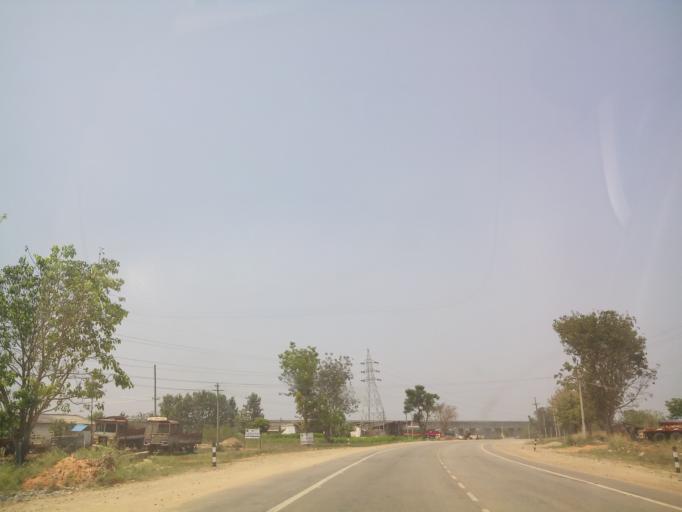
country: IN
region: Karnataka
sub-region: Hassan
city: Hassan
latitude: 12.9887
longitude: 76.0712
